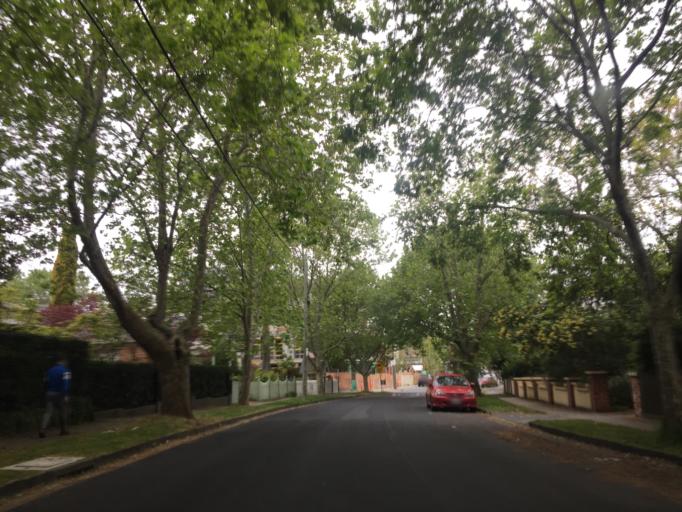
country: AU
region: Victoria
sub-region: Boroondara
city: Kew
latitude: -37.8187
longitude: 145.0346
